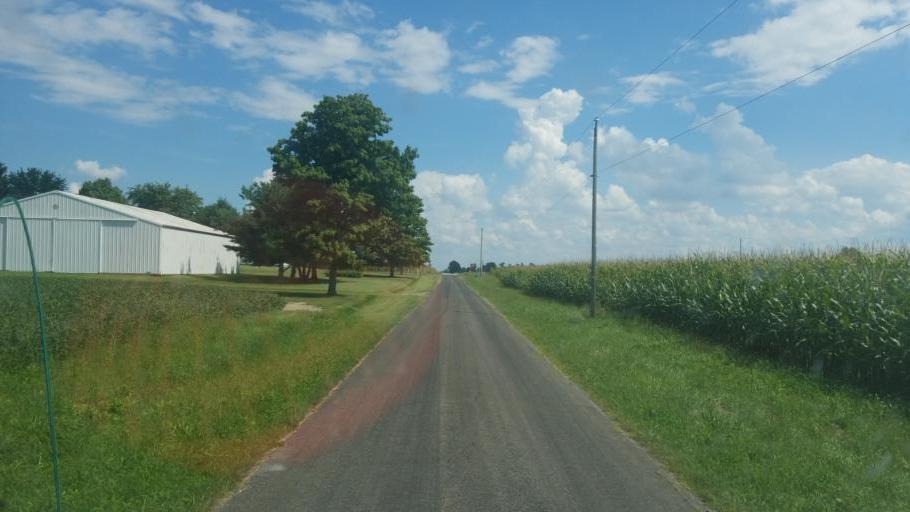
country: US
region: Ohio
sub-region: Hardin County
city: Forest
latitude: 40.8470
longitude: -83.4401
